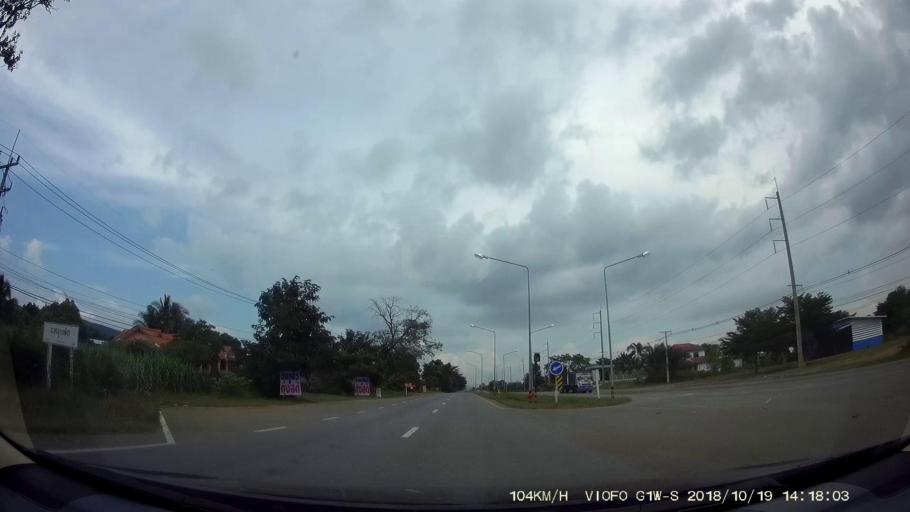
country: TH
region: Chaiyaphum
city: Khon Sawan
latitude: 16.0110
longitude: 102.2313
